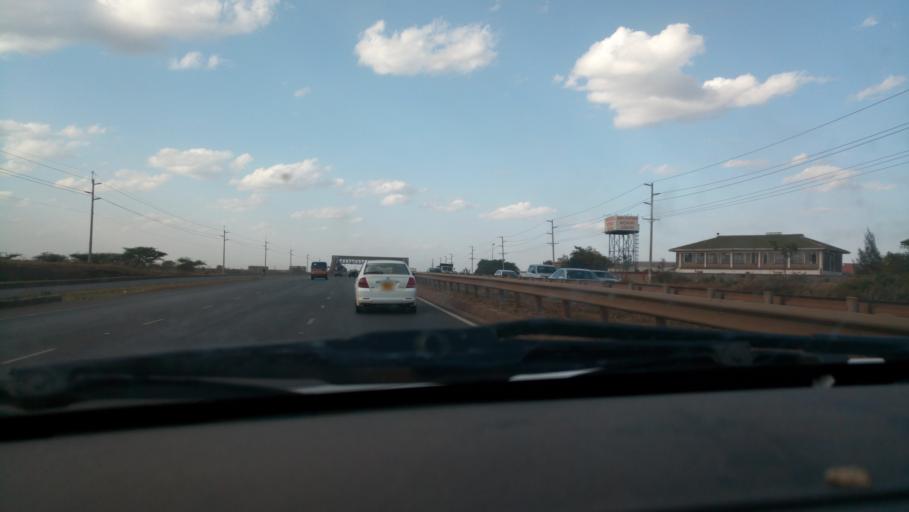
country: KE
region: Nairobi Area
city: Thika
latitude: -1.0569
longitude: 37.0556
